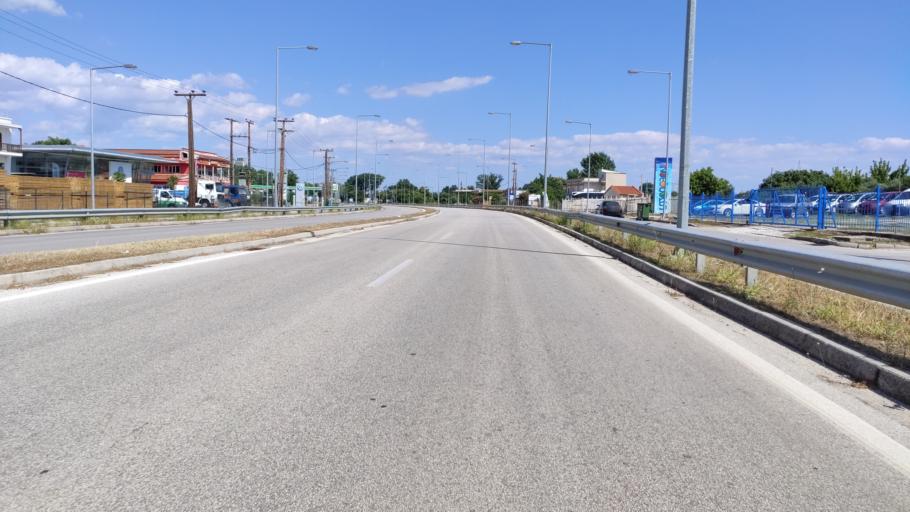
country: GR
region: East Macedonia and Thrace
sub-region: Nomos Rodopis
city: Komotini
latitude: 41.1140
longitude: 25.3815
